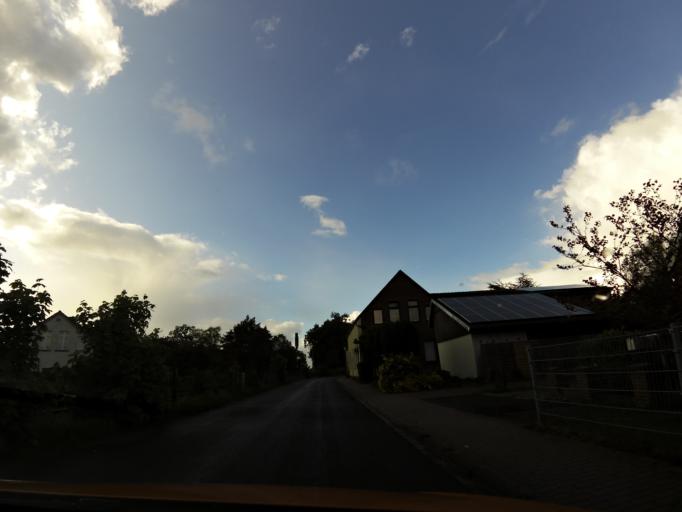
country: DE
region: Lower Saxony
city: Oldenburg
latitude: 53.1340
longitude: 8.2365
